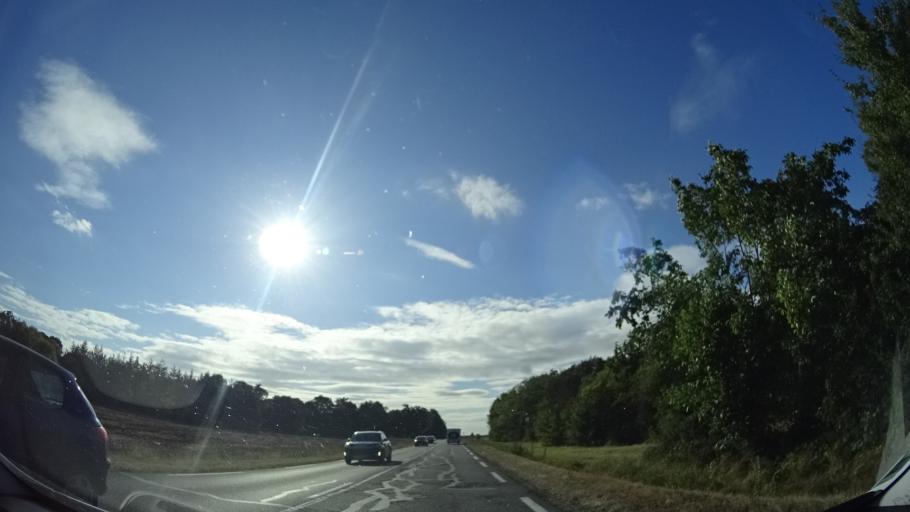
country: FR
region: Centre
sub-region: Departement du Loiret
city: Epieds-en-Beauce
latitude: 47.9335
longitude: 1.6641
